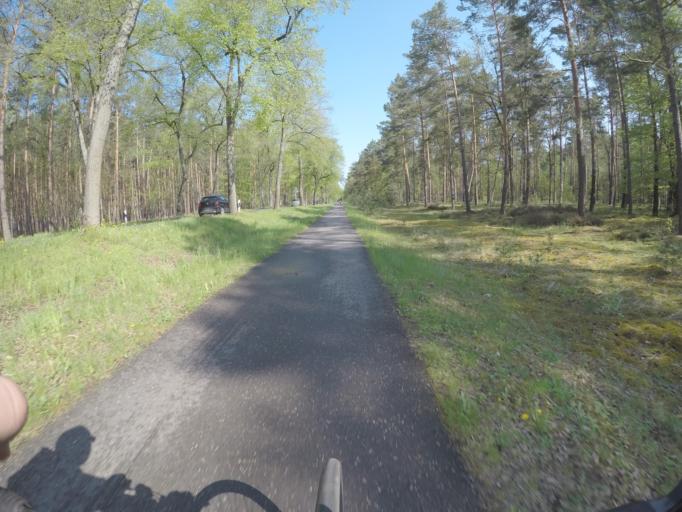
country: DE
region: Brandenburg
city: Wandlitz
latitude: 52.6959
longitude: 13.4429
